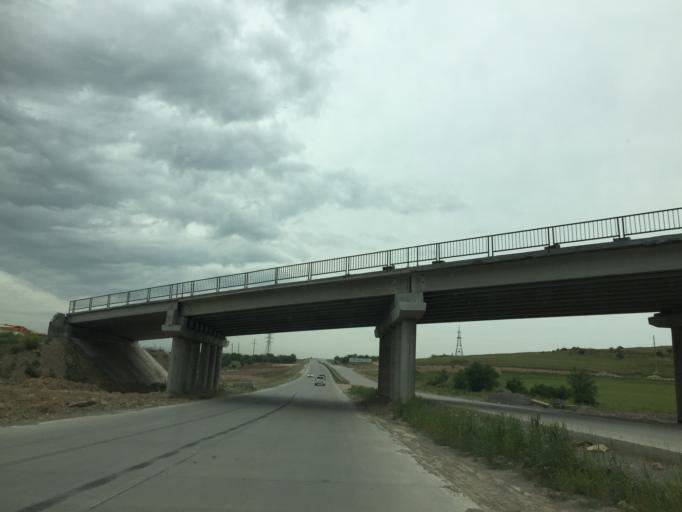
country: KZ
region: Ongtustik Qazaqstan
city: Sastobe
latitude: 42.5306
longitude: 70.0200
